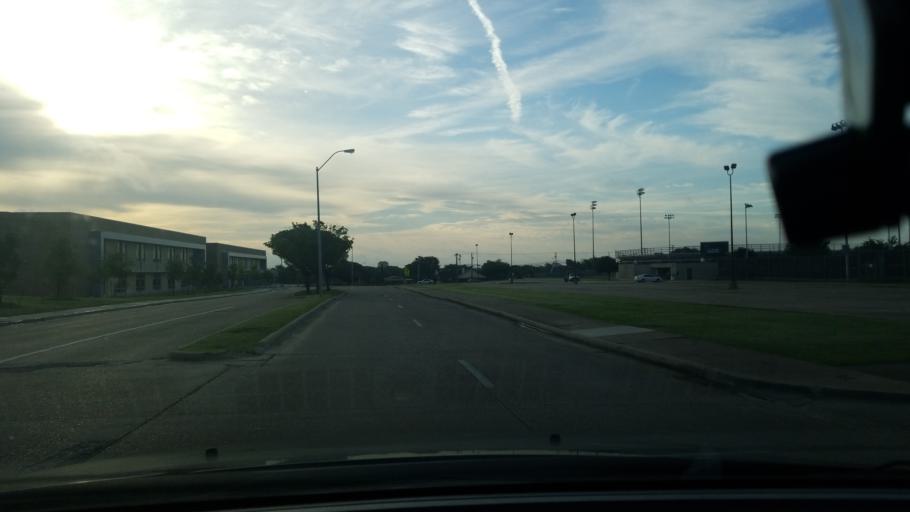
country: US
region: Texas
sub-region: Dallas County
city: Mesquite
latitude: 32.7623
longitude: -96.6342
